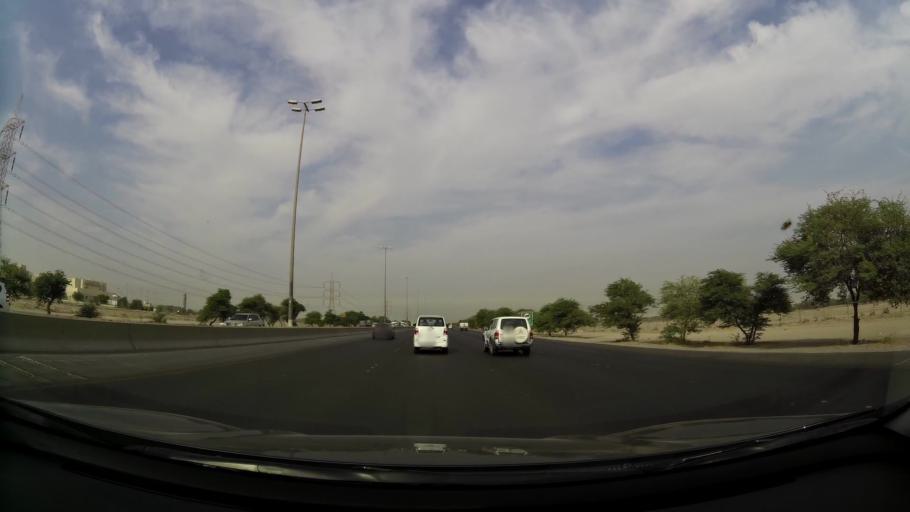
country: KW
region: Al Asimah
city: Ar Rabiyah
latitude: 29.2681
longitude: 47.8271
